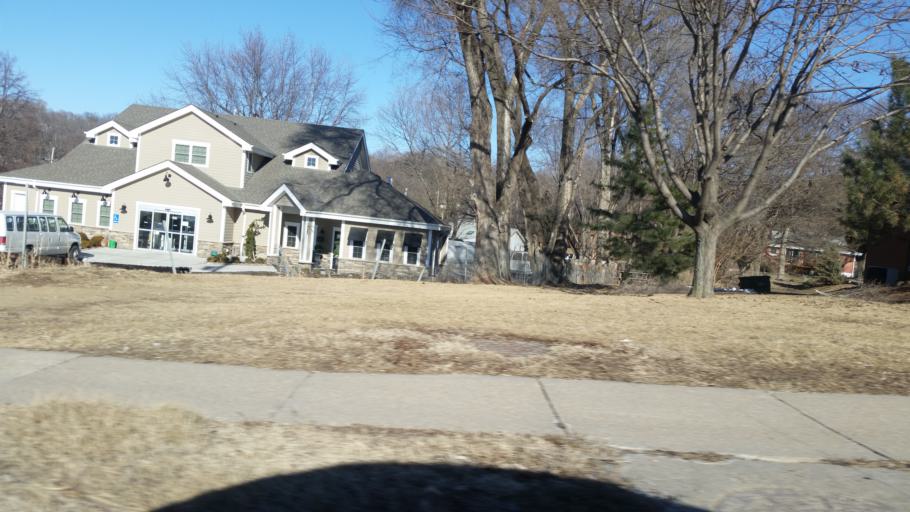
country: US
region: Nebraska
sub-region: Sarpy County
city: Bellevue
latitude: 41.1625
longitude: -95.9220
